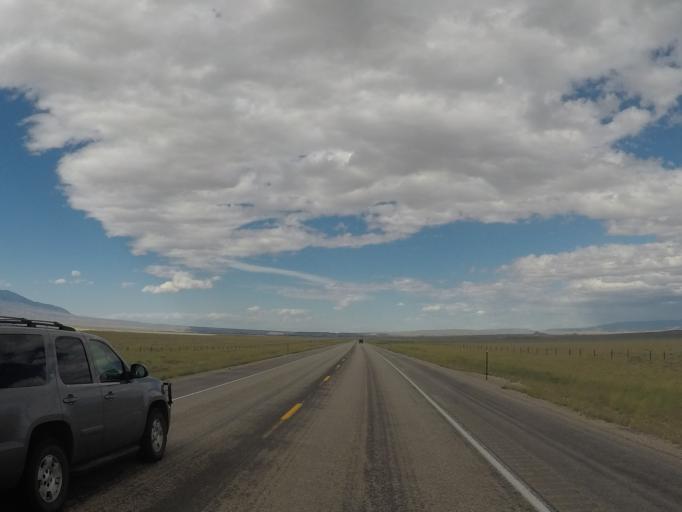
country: US
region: Wyoming
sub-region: Park County
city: Cody
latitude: 44.7895
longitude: -109.1793
